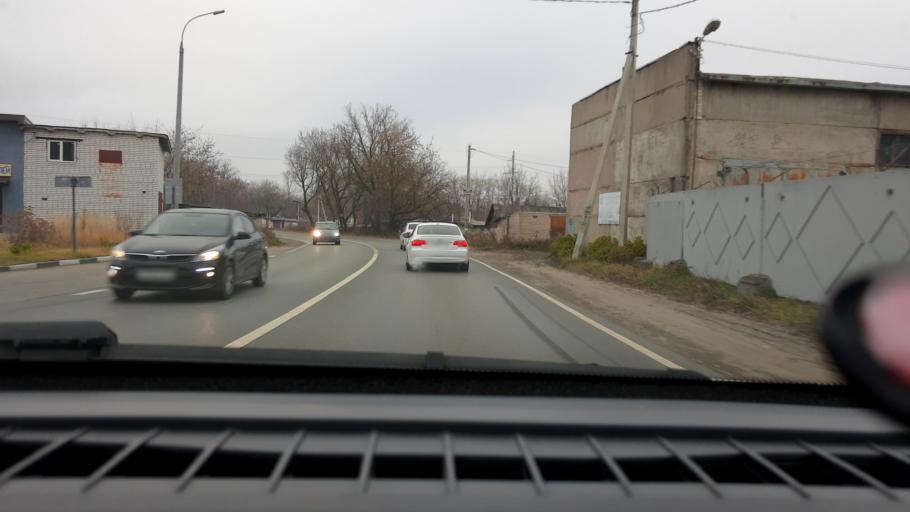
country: RU
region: Nizjnij Novgorod
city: Novaya Balakhna
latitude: 56.5056
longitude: 43.5924
